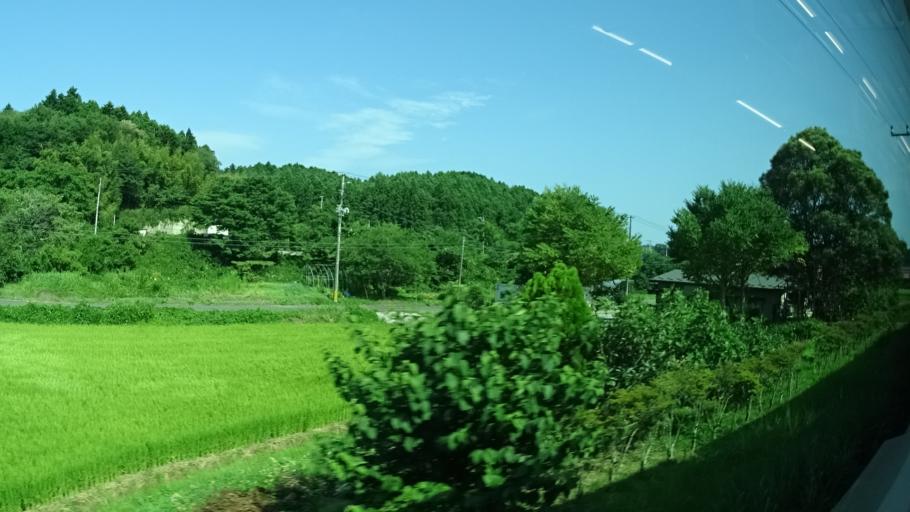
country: JP
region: Miyagi
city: Matsushima
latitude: 38.4034
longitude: 141.0653
